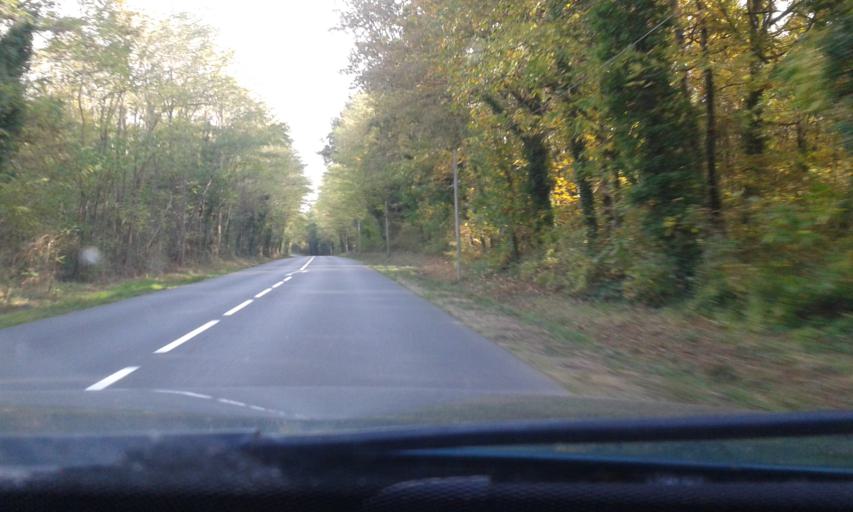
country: FR
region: Centre
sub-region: Departement du Loiret
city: Olivet
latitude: 47.8331
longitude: 1.8703
